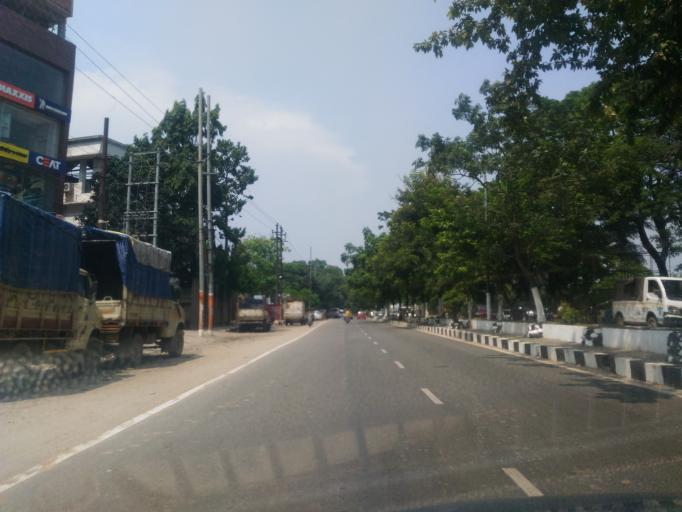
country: IN
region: Assam
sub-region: Kamrup
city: North Guwahati
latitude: 26.1683
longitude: 91.7212
